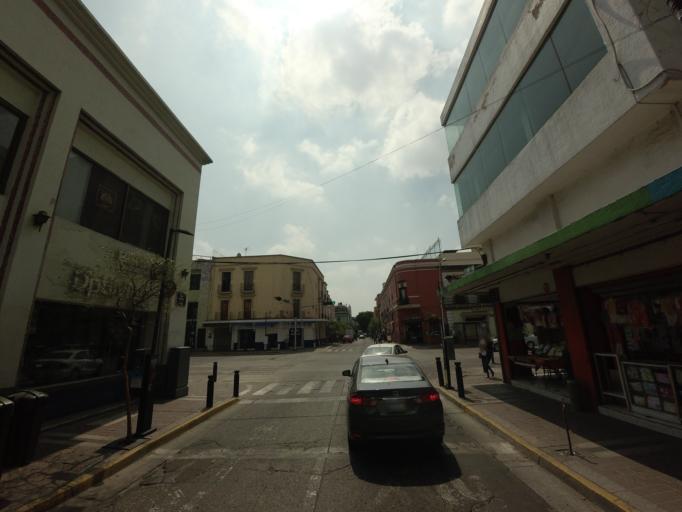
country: MX
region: Jalisco
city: Guadalajara
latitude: 20.6789
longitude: -103.3478
